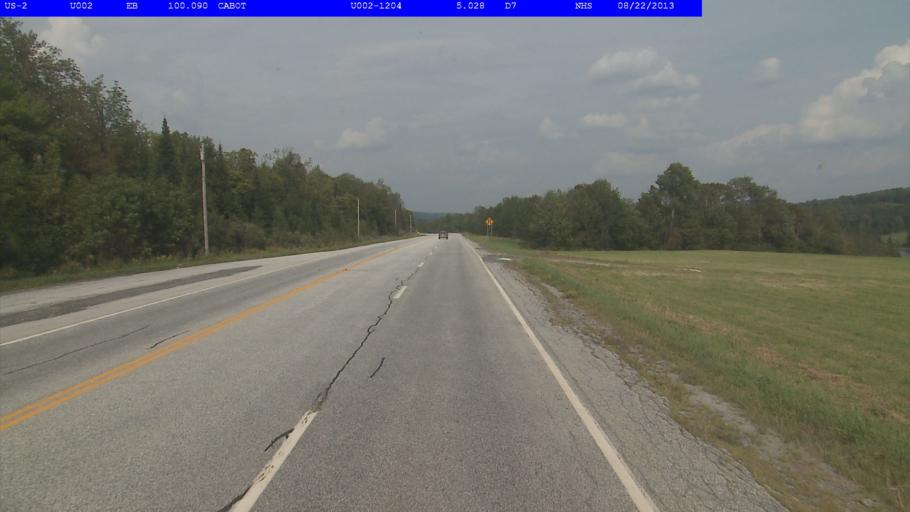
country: US
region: Vermont
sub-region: Caledonia County
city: Hardwick
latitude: 44.3923
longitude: -72.2445
